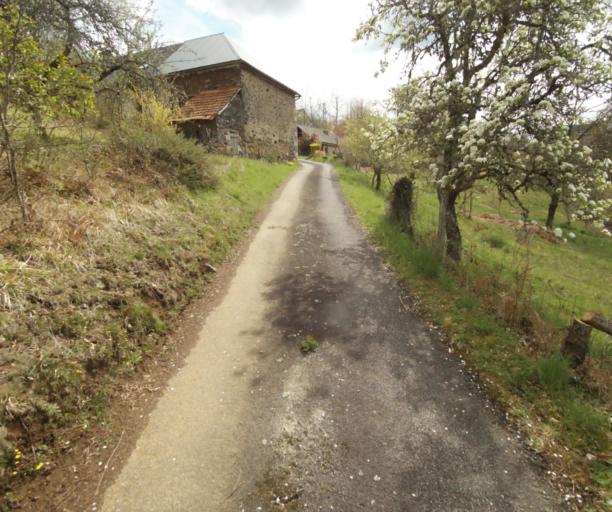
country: FR
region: Limousin
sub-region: Departement de la Correze
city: Laguenne
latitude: 45.2255
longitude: 1.8645
